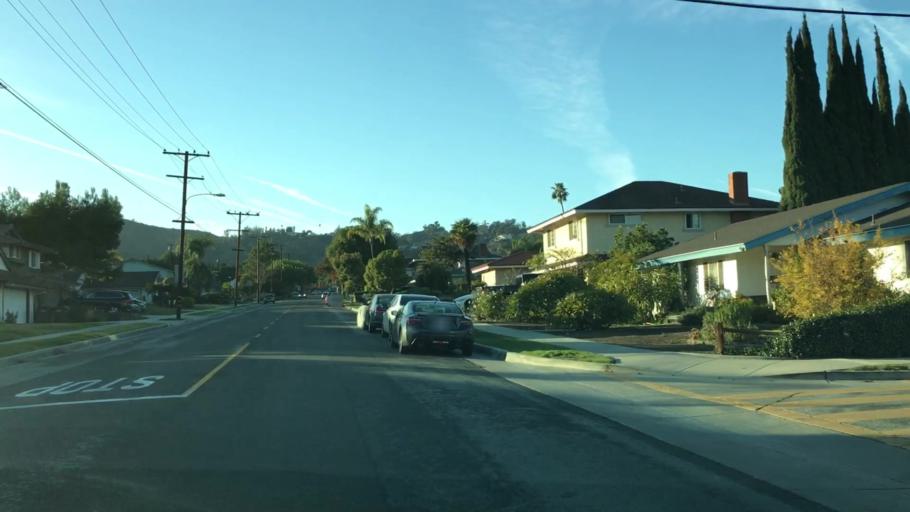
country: US
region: California
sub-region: Los Angeles County
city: Hacienda Heights
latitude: 33.9883
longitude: -117.9783
